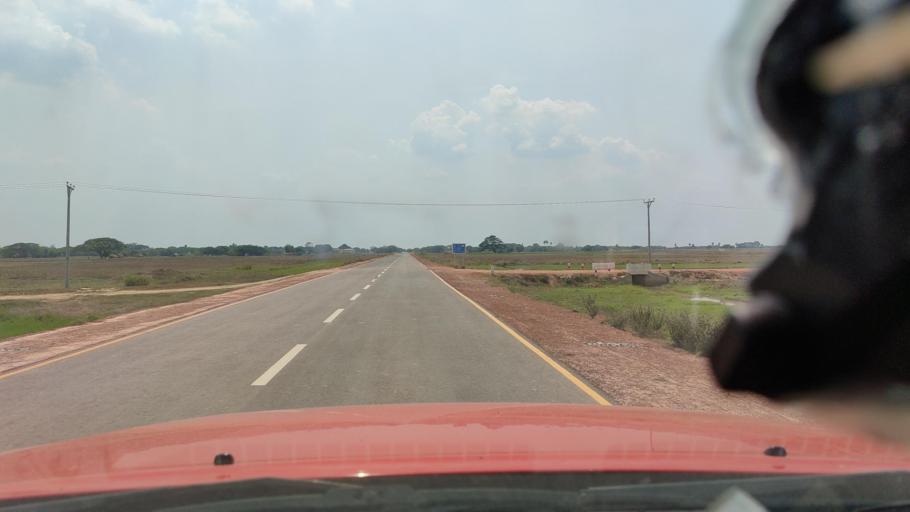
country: MM
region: Bago
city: Thanatpin
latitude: 17.0446
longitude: 96.3631
